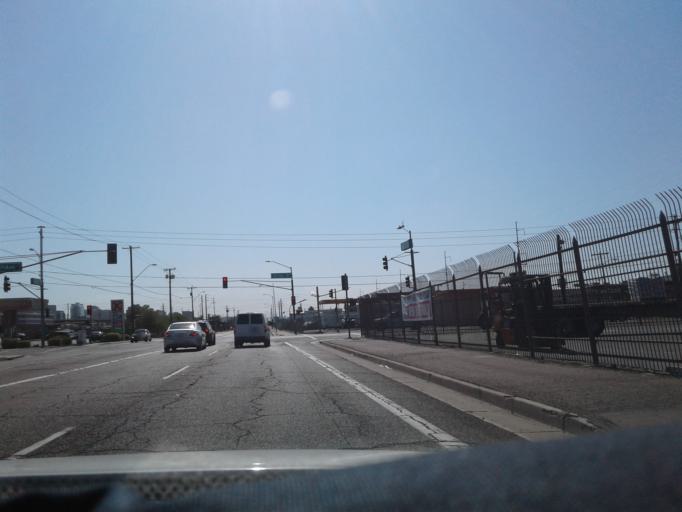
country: US
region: Arizona
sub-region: Maricopa County
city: Phoenix
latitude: 33.4413
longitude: -112.1008
